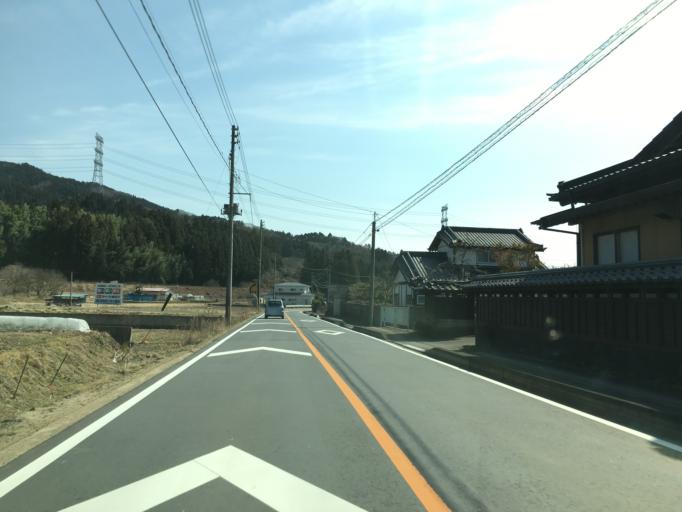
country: JP
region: Ibaraki
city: Daigo
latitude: 36.9369
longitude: 140.4143
